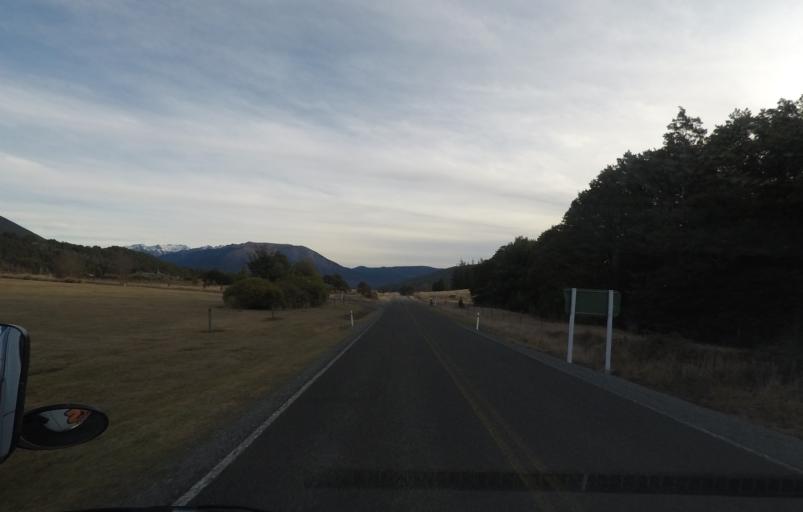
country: NZ
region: Tasman
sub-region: Tasman District
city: Wakefield
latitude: -41.7865
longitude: 172.8902
